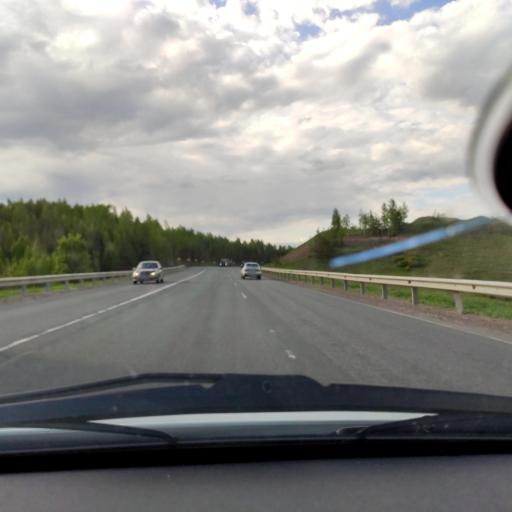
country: RU
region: Bashkortostan
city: Kushnarenkovo
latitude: 55.1624
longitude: 55.1266
